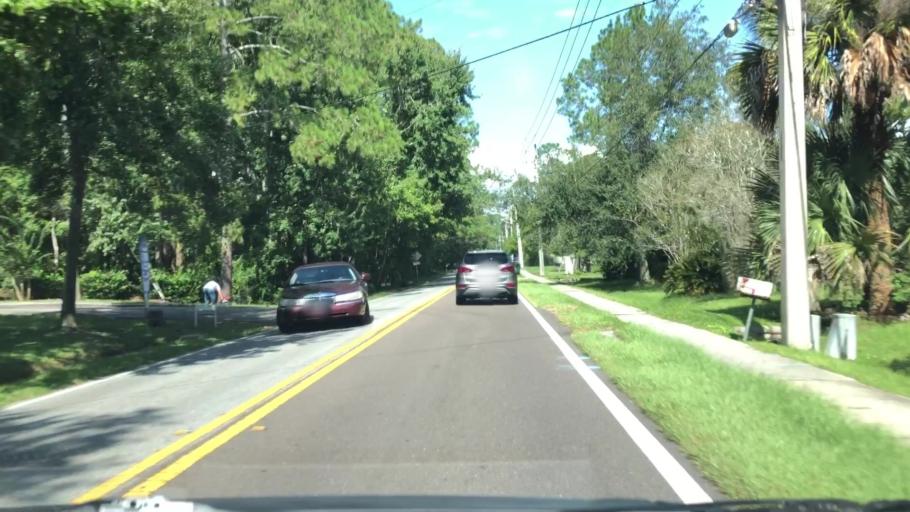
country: US
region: Florida
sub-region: Saint Johns County
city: Fruit Cove
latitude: 30.1848
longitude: -81.6141
